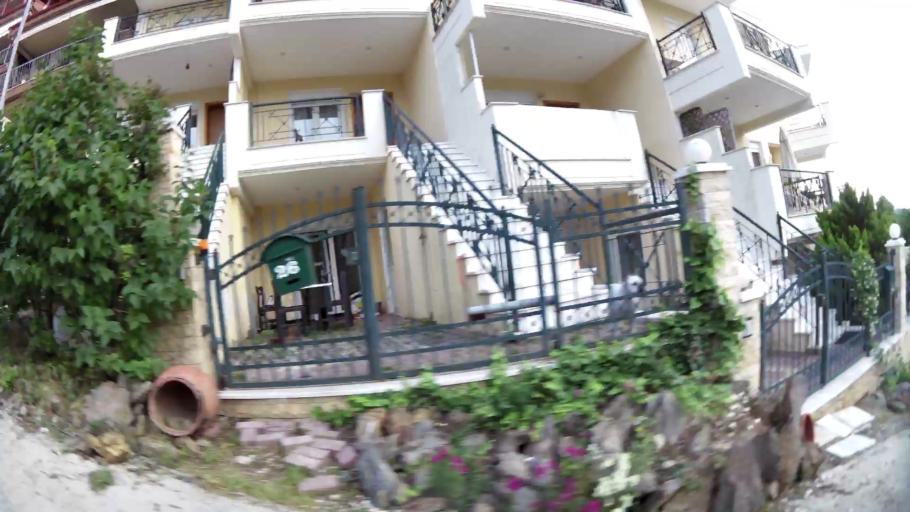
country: GR
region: Central Macedonia
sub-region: Nomos Thessalonikis
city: Pefka
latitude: 40.6601
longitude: 23.0030
